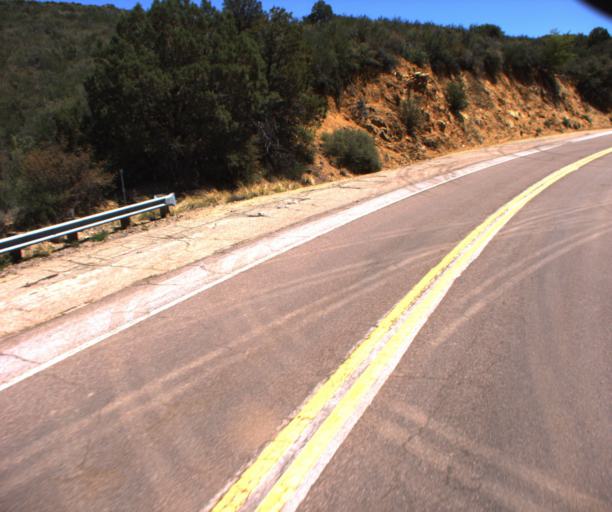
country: US
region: Arizona
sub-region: Yavapai County
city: Prescott
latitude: 34.4542
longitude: -112.5296
